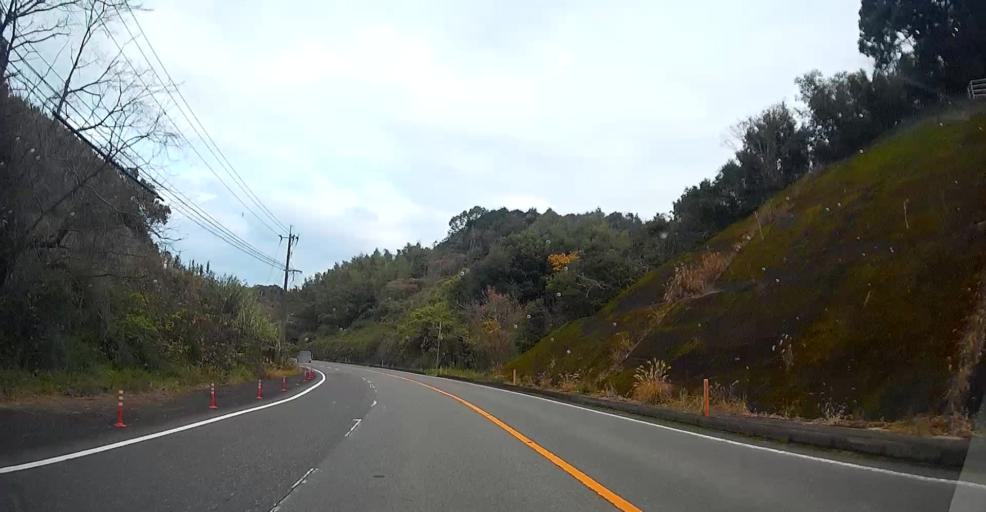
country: JP
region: Kumamoto
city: Hondo
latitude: 32.4950
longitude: 130.2986
